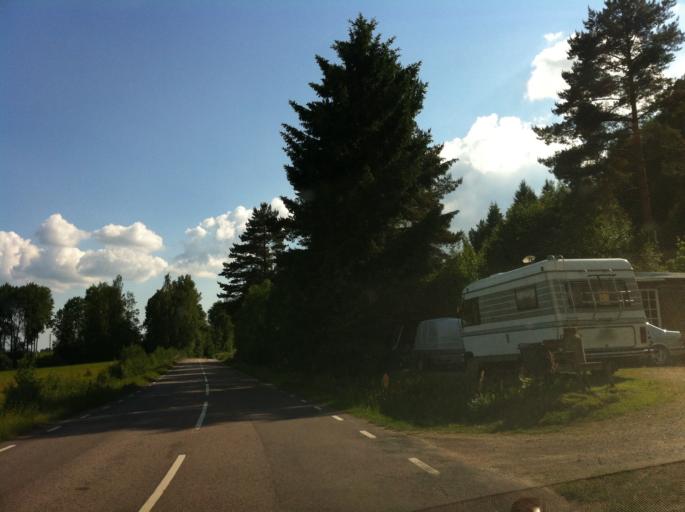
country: SE
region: Vaermland
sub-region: Kils Kommun
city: Kil
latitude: 59.5835
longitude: 13.3103
